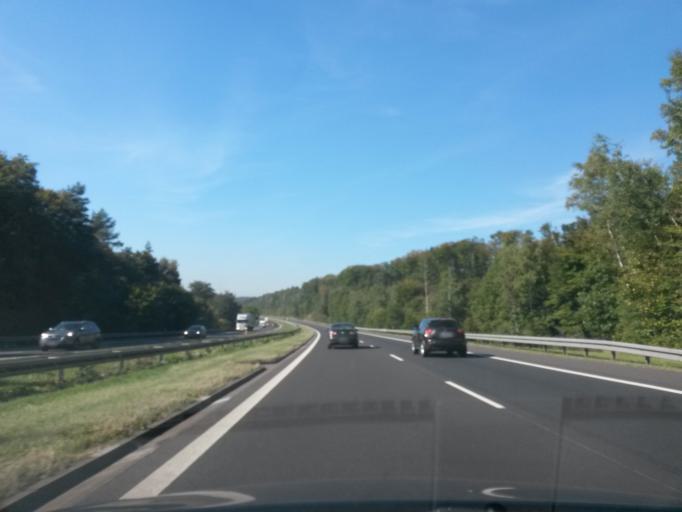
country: PL
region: Lesser Poland Voivodeship
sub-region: Powiat krakowski
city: Czulow
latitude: 50.0931
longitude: 19.6814
